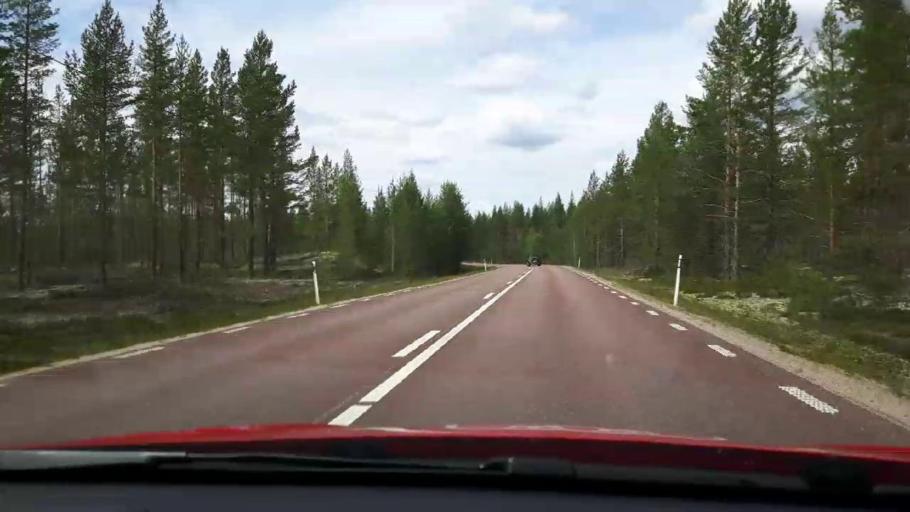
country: SE
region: Jaemtland
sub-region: Harjedalens Kommun
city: Sveg
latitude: 62.0580
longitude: 14.5897
